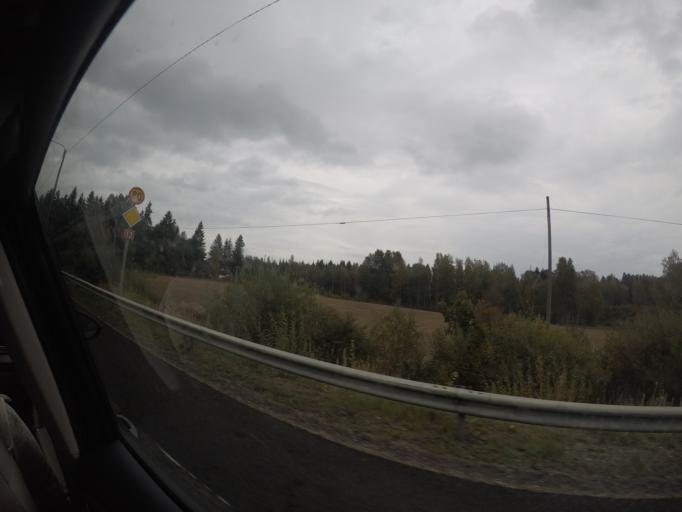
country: FI
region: Pirkanmaa
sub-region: Tampere
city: Kangasala
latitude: 61.4416
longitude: 24.1194
